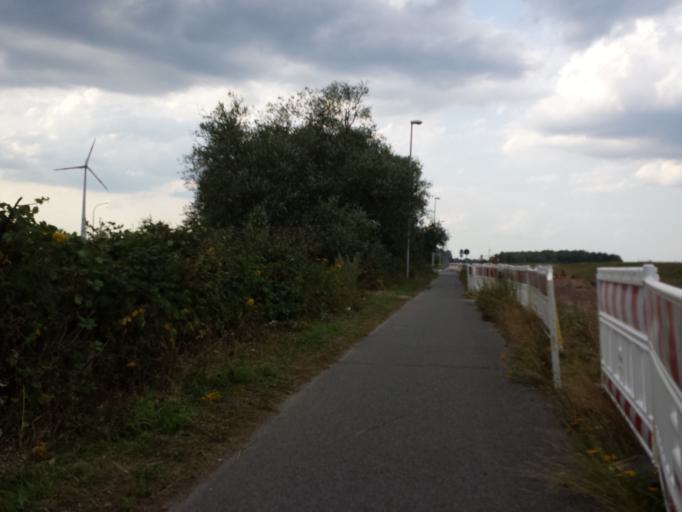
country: DE
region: Lower Saxony
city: Stuhr
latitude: 53.0972
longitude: 8.7276
